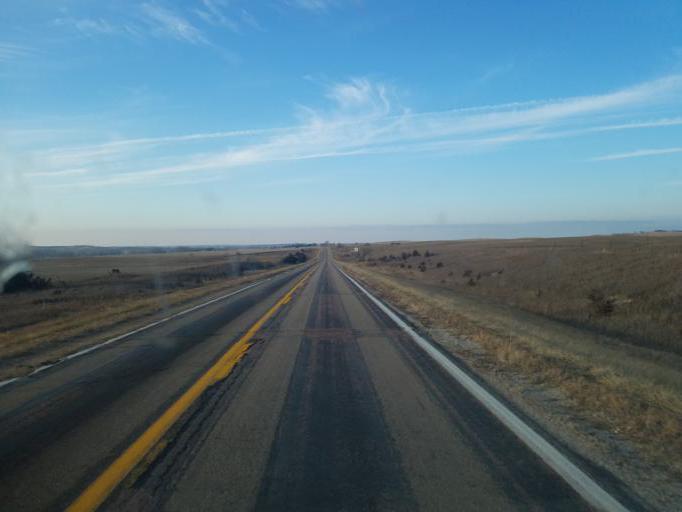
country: US
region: Nebraska
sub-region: Cedar County
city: Hartington
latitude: 42.7215
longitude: -97.1232
